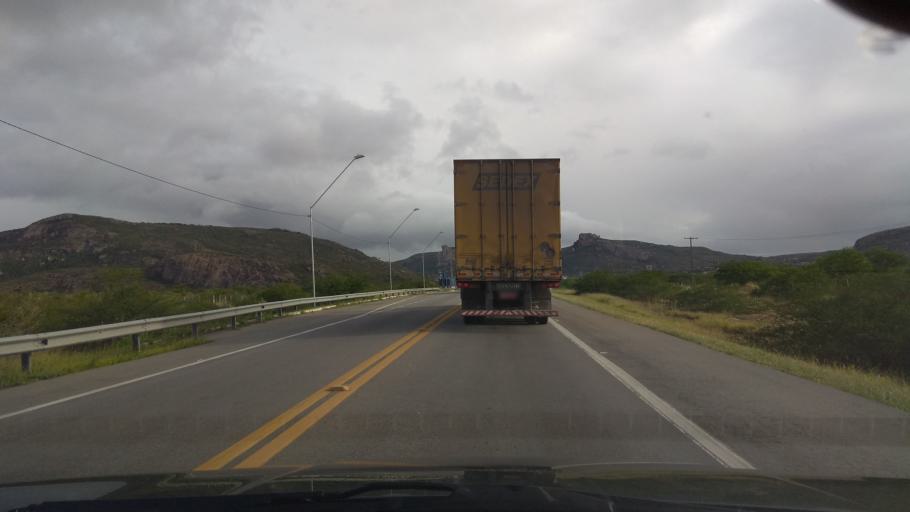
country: BR
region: Bahia
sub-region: Amargosa
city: Amargosa
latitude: -12.8478
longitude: -39.8418
